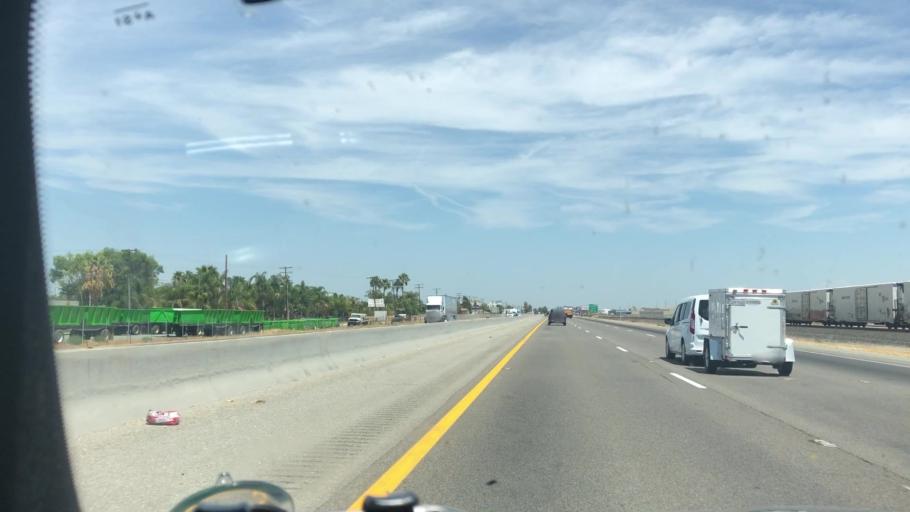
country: US
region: California
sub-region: Kern County
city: Delano
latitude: 35.7321
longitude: -119.2397
